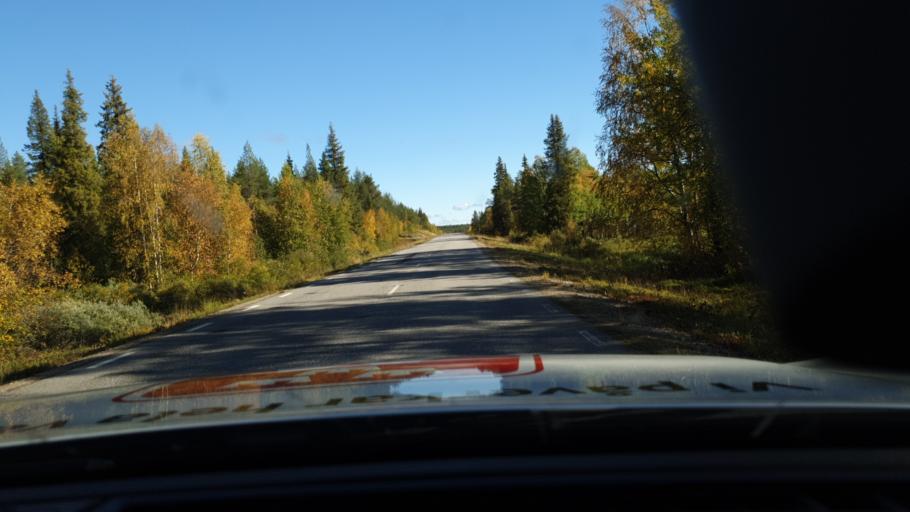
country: FI
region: Lapland
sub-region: Tunturi-Lappi
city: Muonio
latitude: 67.9304
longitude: 23.3591
